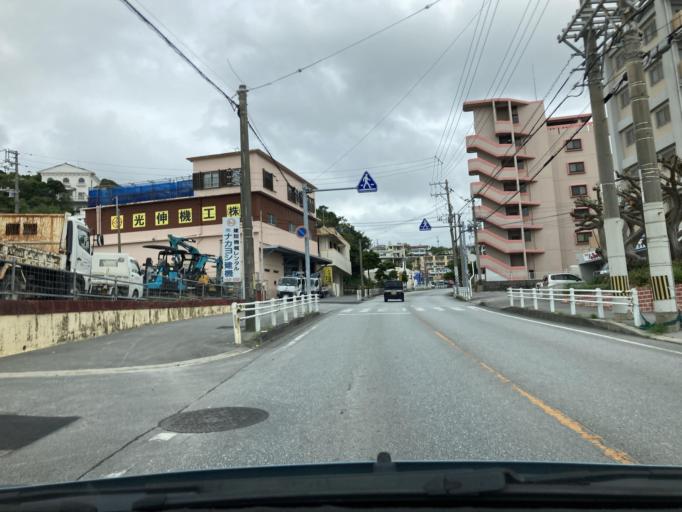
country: JP
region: Okinawa
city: Ginowan
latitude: 26.2332
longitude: 127.7525
